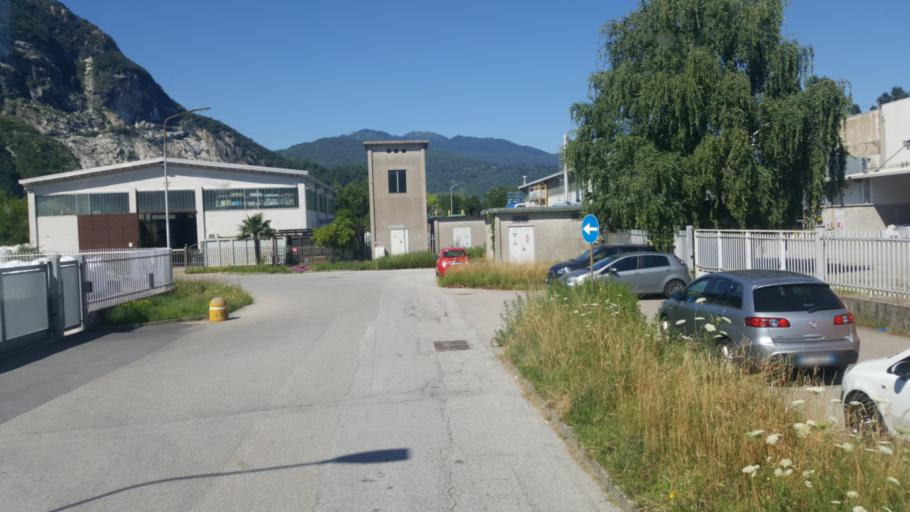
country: IT
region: Piedmont
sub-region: Provincia Verbano-Cusio-Ossola
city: Gravellona Toce
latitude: 45.9308
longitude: 8.4569
